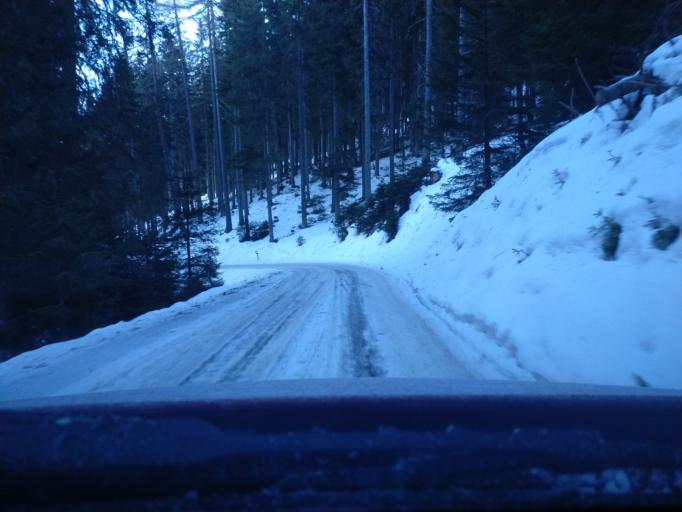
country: AT
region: Carinthia
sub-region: Politischer Bezirk Villach Land
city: Arriach
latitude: 46.7007
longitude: 13.8991
